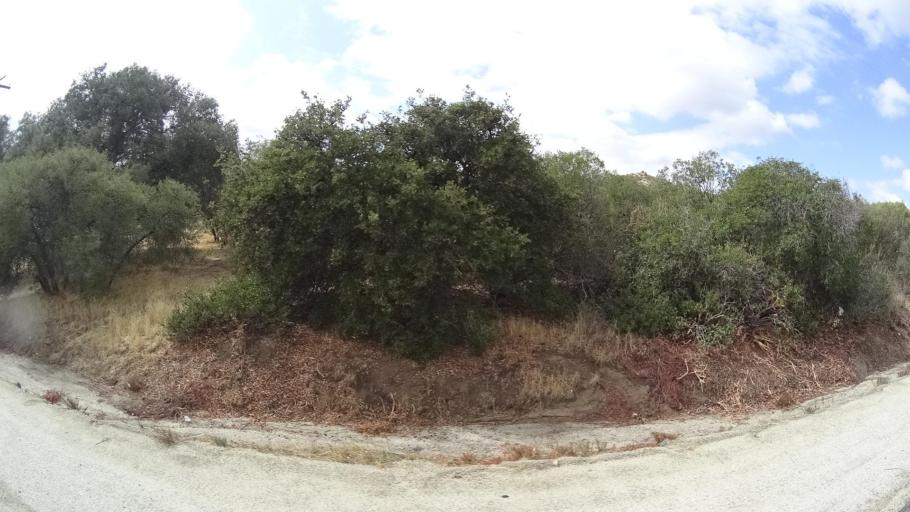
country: US
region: California
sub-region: San Diego County
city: Campo
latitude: 32.6710
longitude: -116.4884
